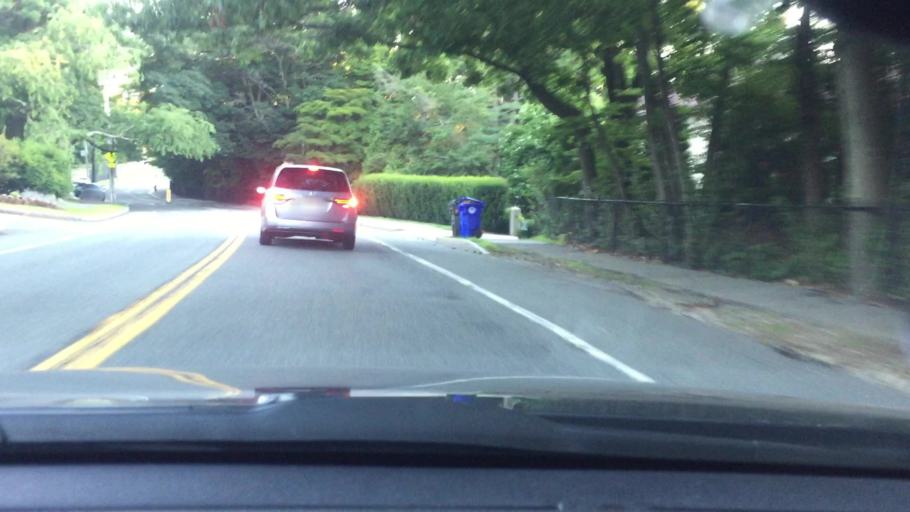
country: US
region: Massachusetts
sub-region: Suffolk County
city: Jamaica Plain
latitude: 42.3130
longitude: -71.1386
